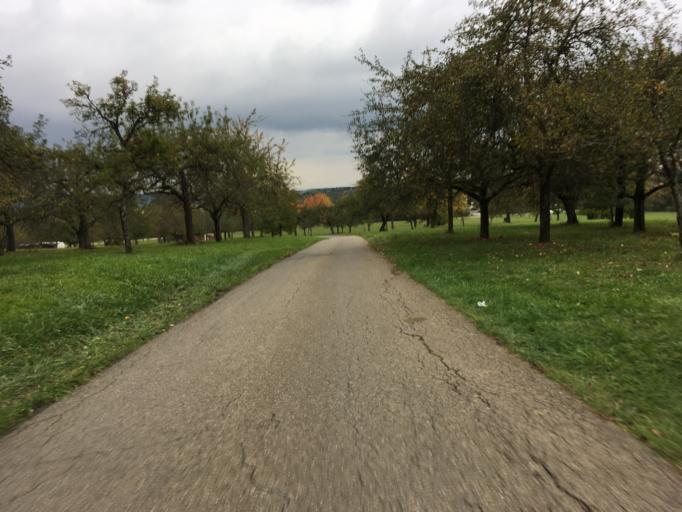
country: DE
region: Baden-Wuerttemberg
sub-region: Tuebingen Region
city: Gomaringen
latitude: 48.4450
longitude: 9.0931
